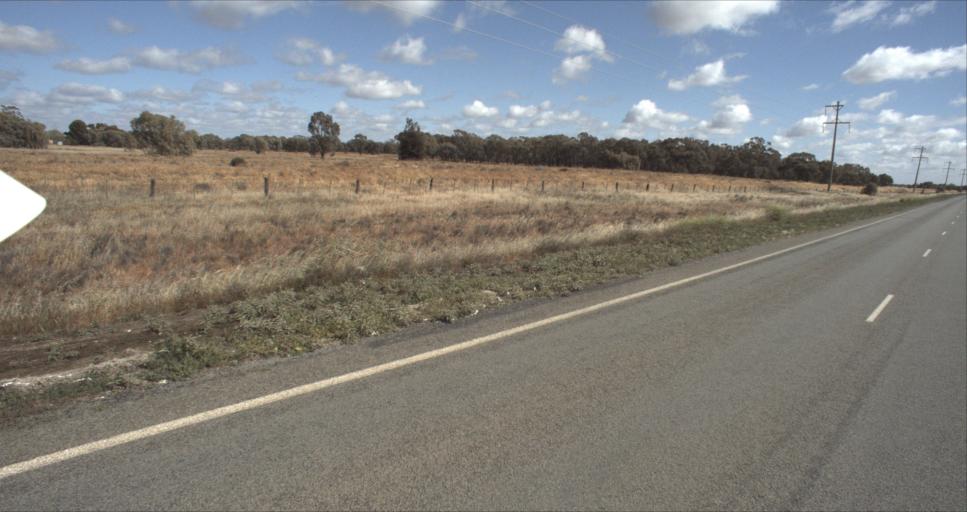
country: AU
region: New South Wales
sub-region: Murrumbidgee Shire
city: Darlington Point
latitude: -34.5475
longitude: 146.1711
